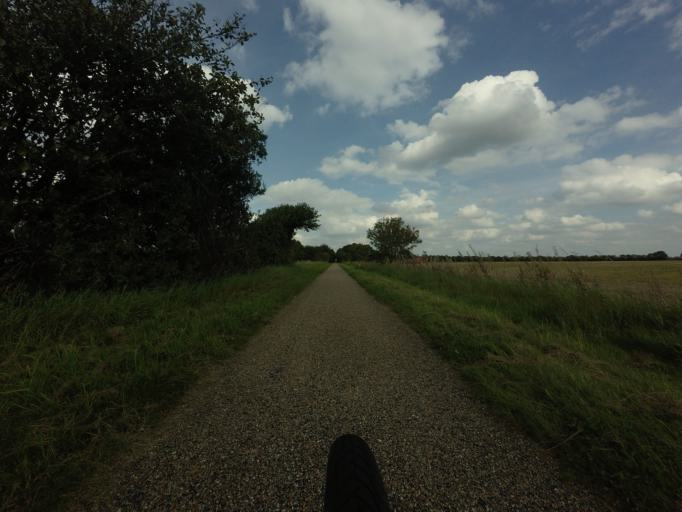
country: DK
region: Central Jutland
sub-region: Herning Kommune
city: Sunds
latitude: 56.2238
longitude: 9.0663
